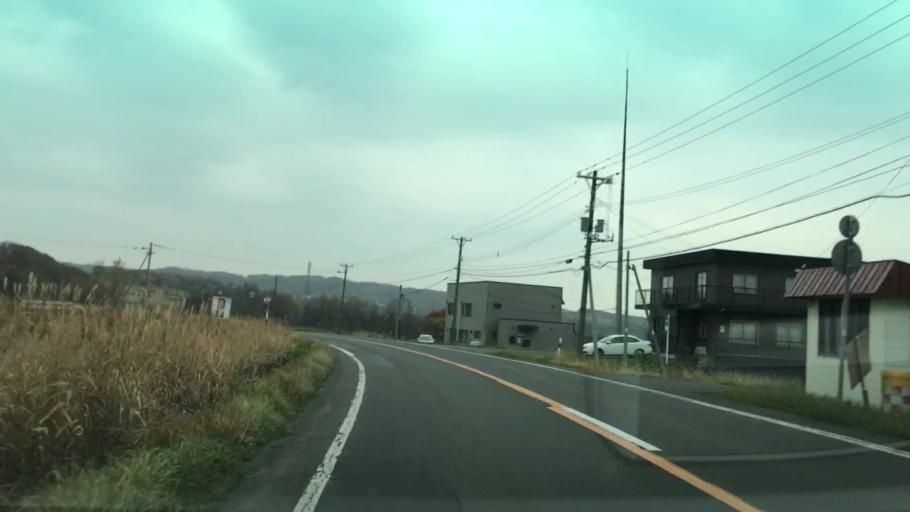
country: JP
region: Hokkaido
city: Ishikari
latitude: 43.3655
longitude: 141.4278
